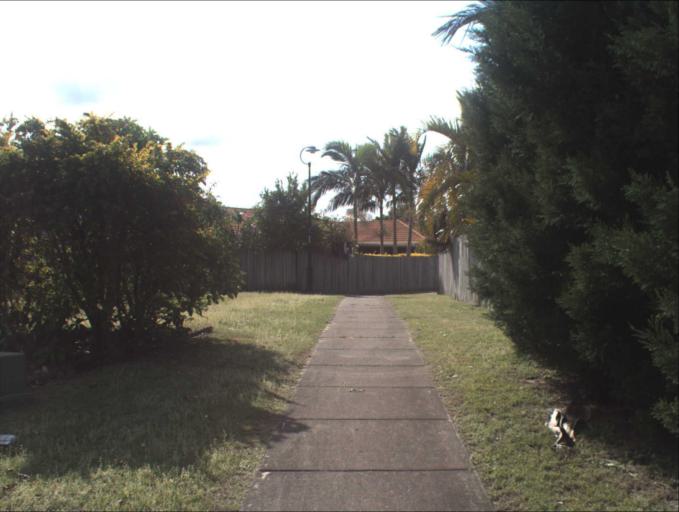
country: AU
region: Queensland
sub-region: Logan
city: Park Ridge South
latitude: -27.6884
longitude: 153.0541
